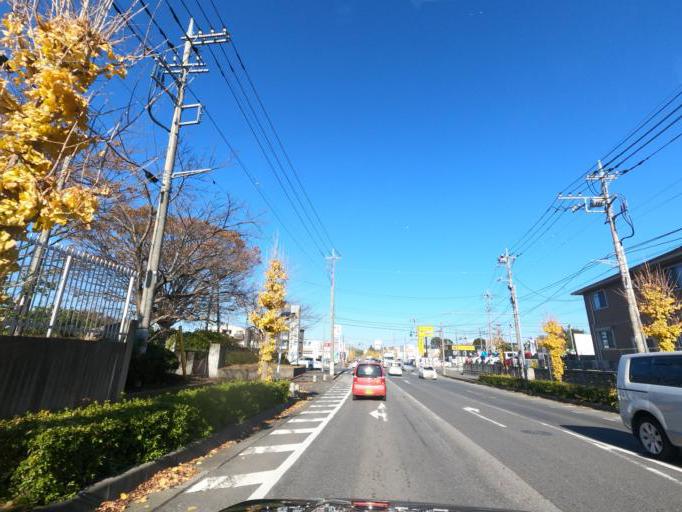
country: JP
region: Ibaraki
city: Mitsukaido
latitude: 35.9816
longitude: 139.9770
